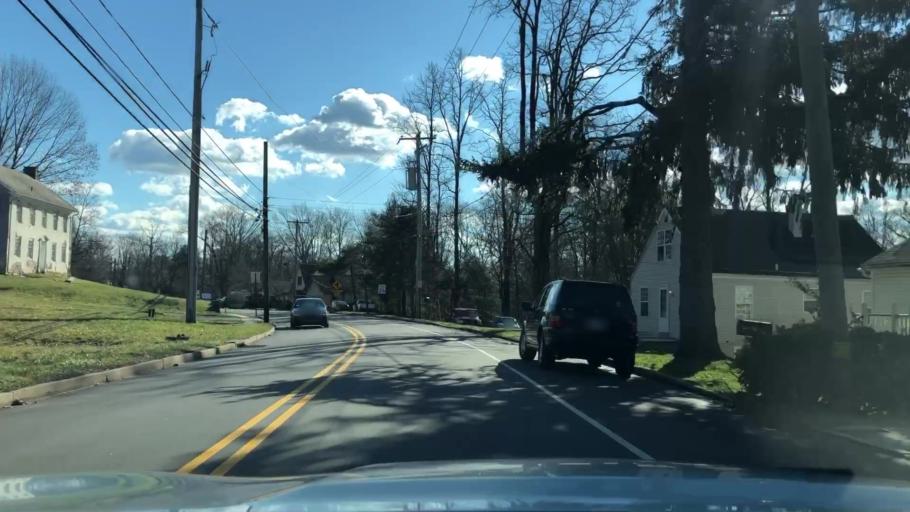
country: US
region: Pennsylvania
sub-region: Montgomery County
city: Pottstown
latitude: 40.2604
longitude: -75.6592
